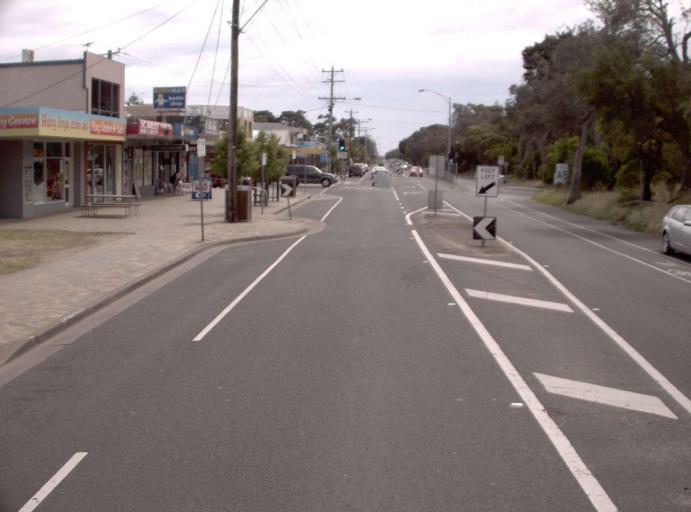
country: AU
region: Victoria
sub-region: Mornington Peninsula
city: Rosebud West
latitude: -38.3634
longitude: 144.8774
